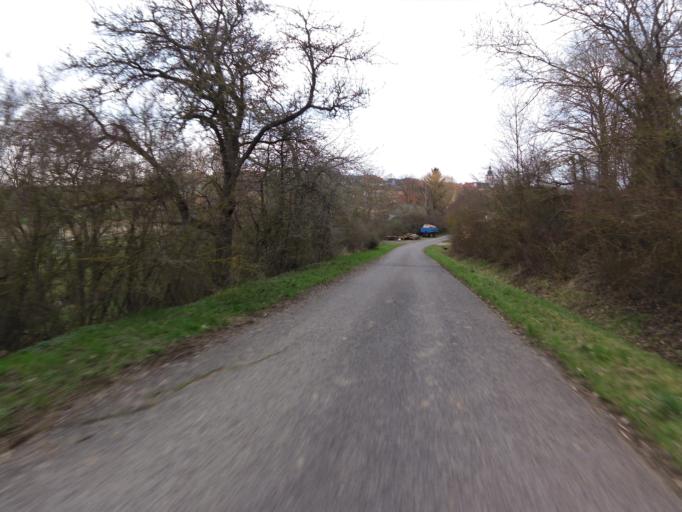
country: DE
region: Bavaria
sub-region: Regierungsbezirk Unterfranken
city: Buchbrunn
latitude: 49.7475
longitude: 10.1180
